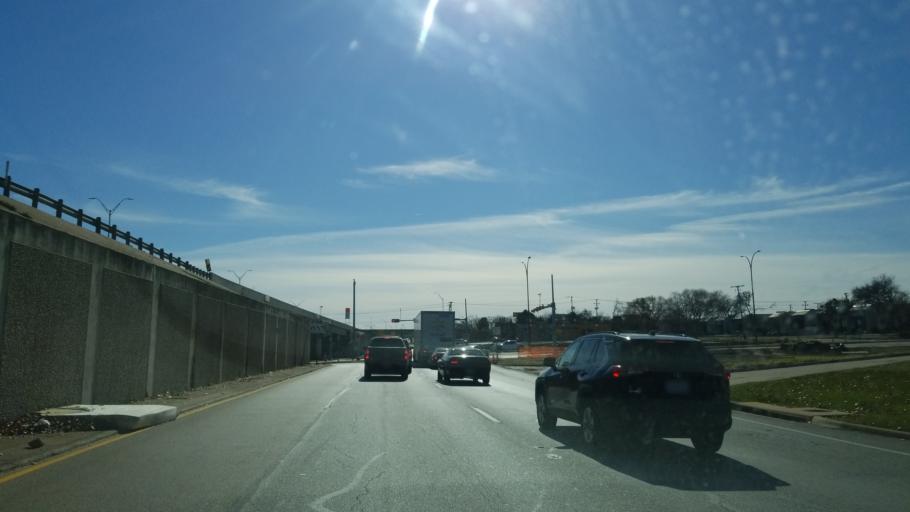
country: US
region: Texas
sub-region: Tarrant County
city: Arlington
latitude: 32.7497
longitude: -97.0632
